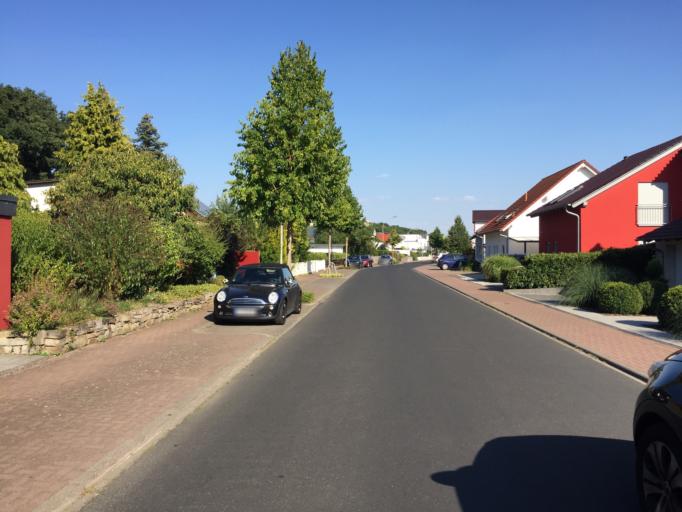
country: DE
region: Hesse
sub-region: Regierungsbezirk Giessen
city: Langgons
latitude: 50.5406
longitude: 8.6685
